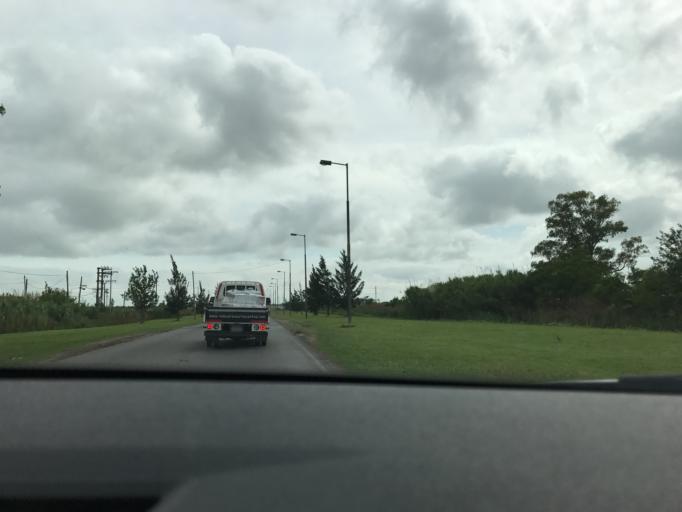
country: AR
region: Buenos Aires
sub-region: Partido de La Plata
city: La Plata
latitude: -34.8440
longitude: -58.0749
